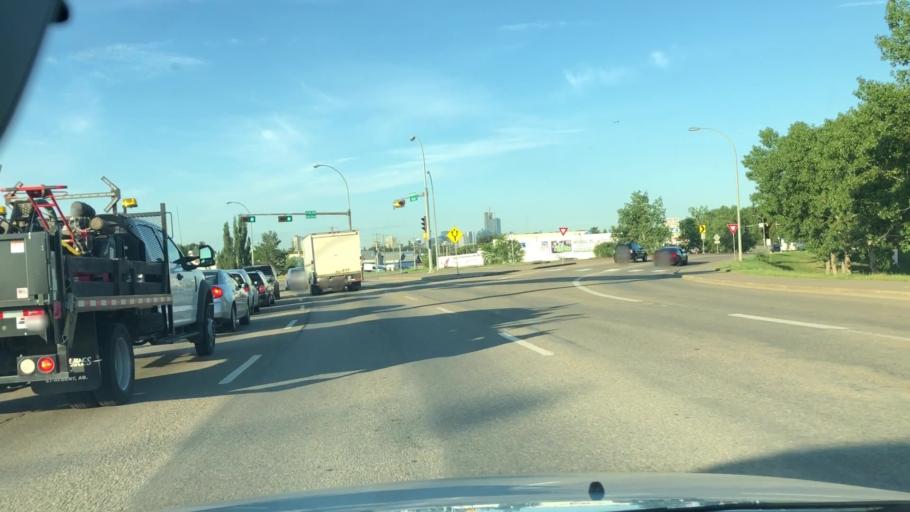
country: CA
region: Alberta
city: Edmonton
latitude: 53.5799
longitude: -113.4542
